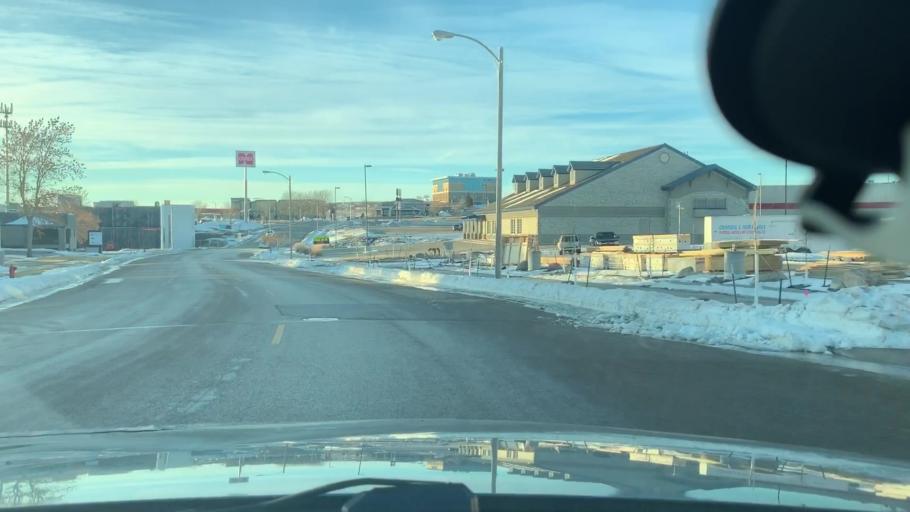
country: US
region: North Dakota
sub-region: Burleigh County
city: Bismarck
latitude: 46.8279
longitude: -100.8111
